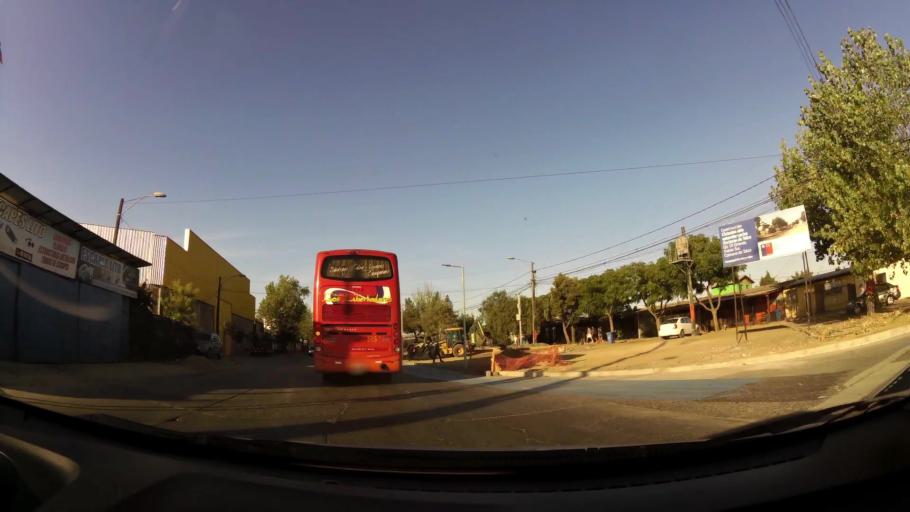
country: CL
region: Maule
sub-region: Provincia de Talca
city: Talca
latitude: -35.4340
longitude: -71.6420
